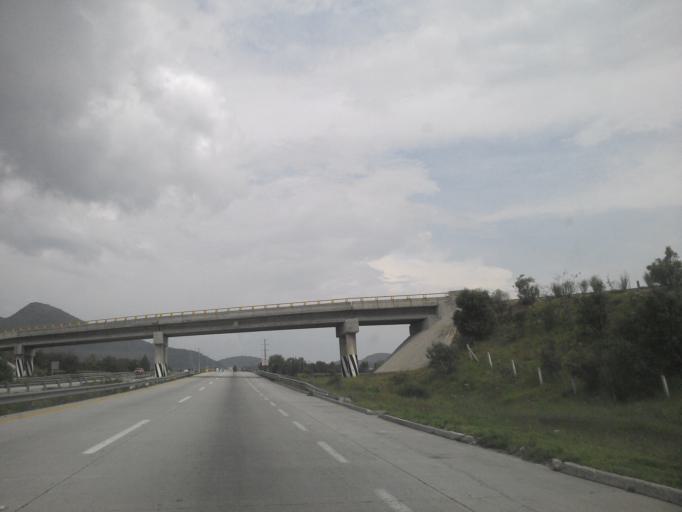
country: MX
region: Hidalgo
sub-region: Atitalaquia
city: Tezoquipa
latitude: 20.0489
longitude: -99.1875
